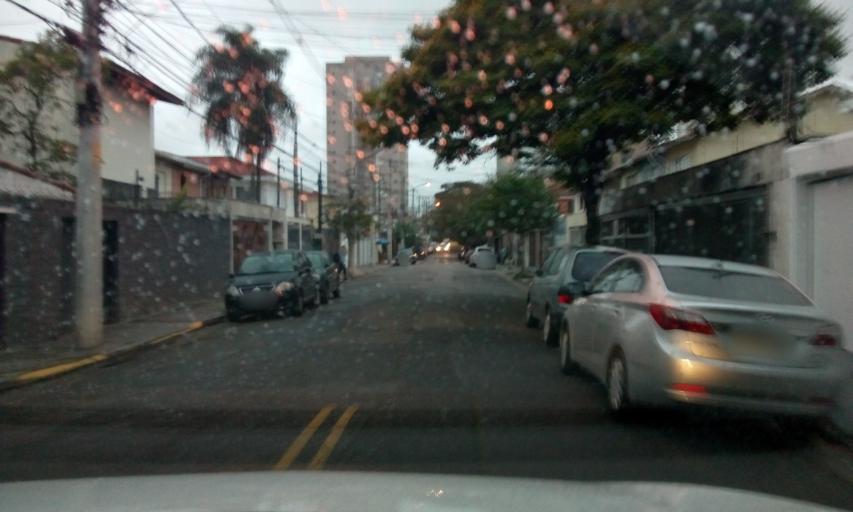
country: BR
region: Sao Paulo
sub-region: Sao Paulo
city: Sao Paulo
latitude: -23.6097
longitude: -46.6905
